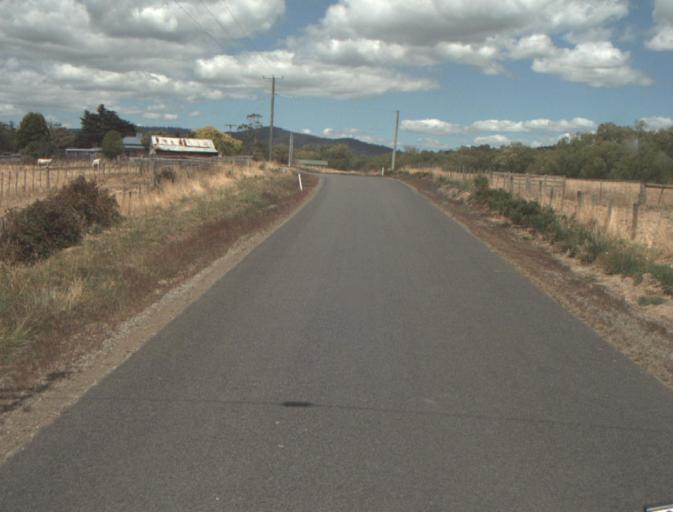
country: AU
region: Tasmania
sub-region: Launceston
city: Mayfield
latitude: -41.2225
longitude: 147.1372
